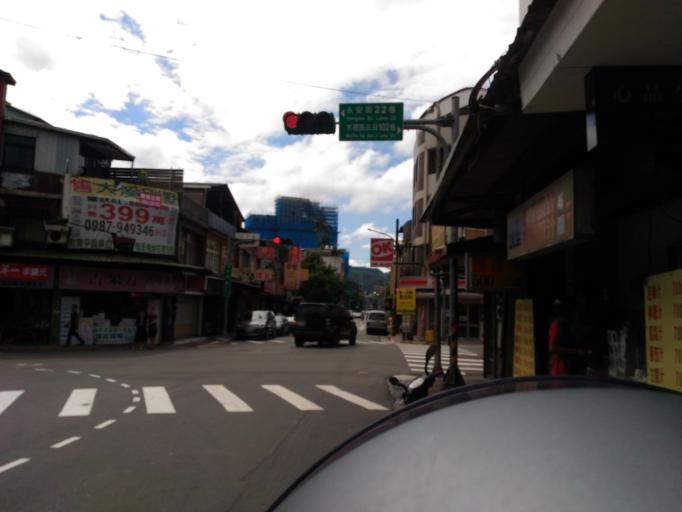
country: TW
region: Taipei
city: Taipei
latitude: 24.9871
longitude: 121.5685
